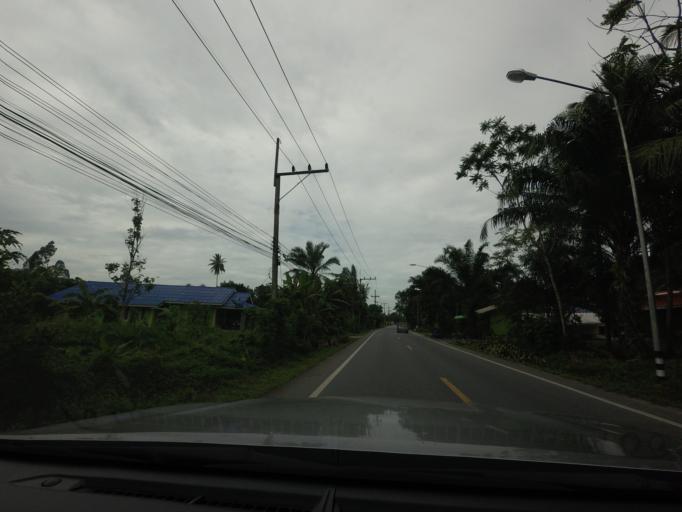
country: TH
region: Nakhon Si Thammarat
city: Phra Phrom
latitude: 8.3159
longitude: 99.9452
